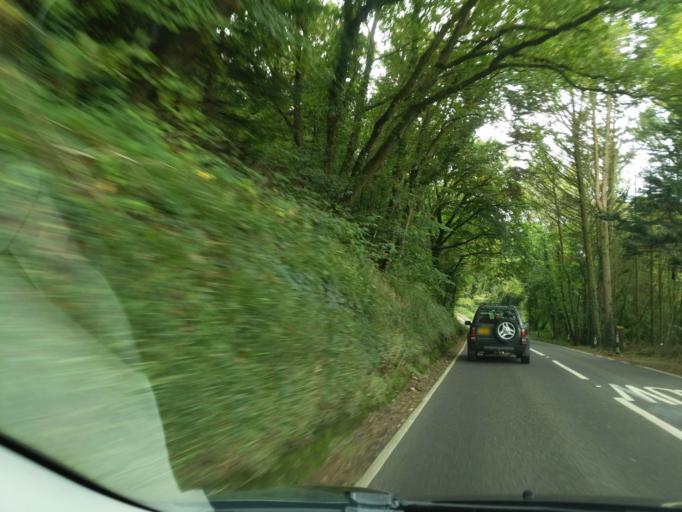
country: GB
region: England
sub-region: Cornwall
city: Wadebridge
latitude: 50.5074
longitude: -4.7850
